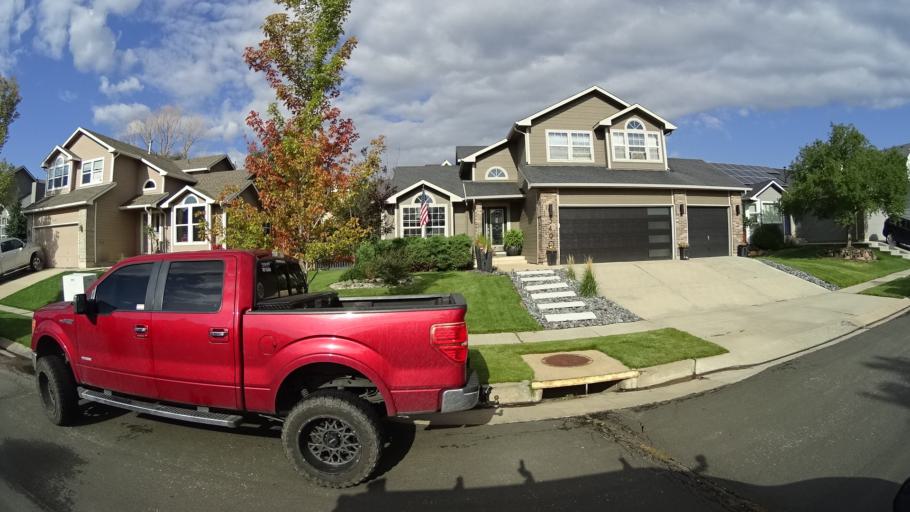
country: US
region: Colorado
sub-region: El Paso County
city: Manitou Springs
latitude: 38.9100
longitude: -104.8617
